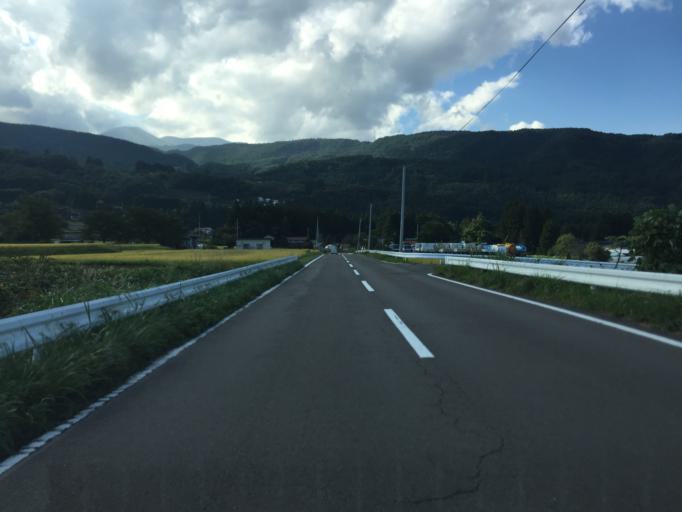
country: JP
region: Fukushima
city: Fukushima-shi
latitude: 37.7110
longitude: 140.3540
